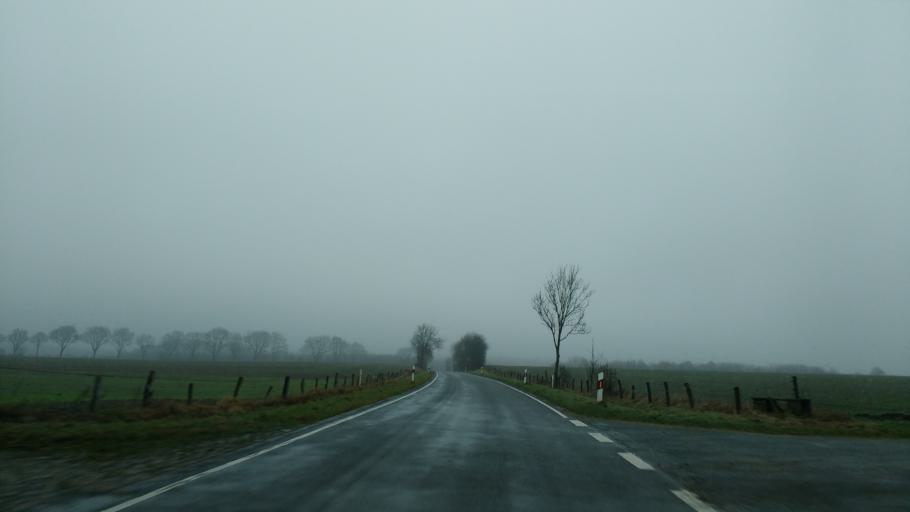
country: DE
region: Schleswig-Holstein
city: Nindorf
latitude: 54.1363
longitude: 9.6931
